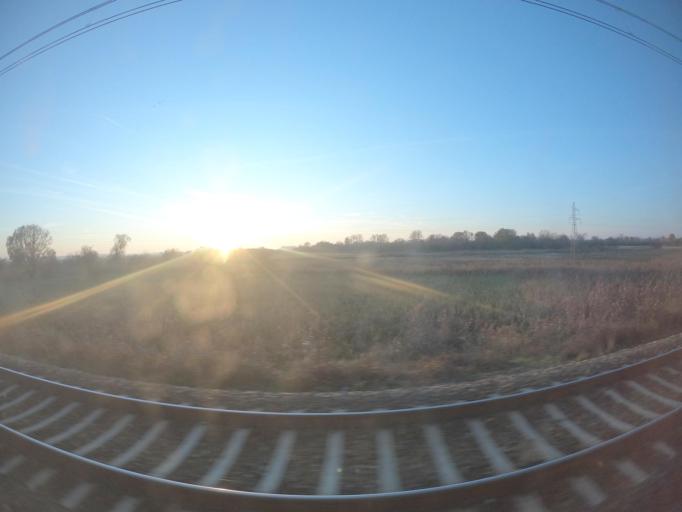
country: PL
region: Lubusz
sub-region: Powiat gorzowski
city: Kostrzyn nad Odra
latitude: 52.5654
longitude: 14.6468
